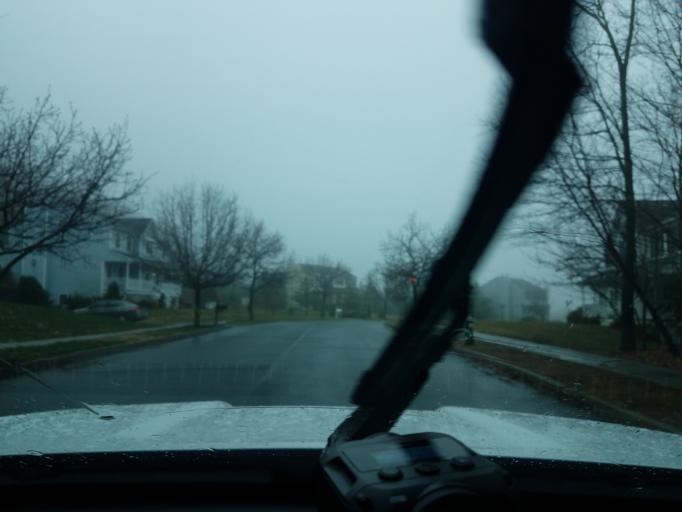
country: US
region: Connecticut
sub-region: New Haven County
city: Naugatuck
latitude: 41.5020
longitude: -73.0328
